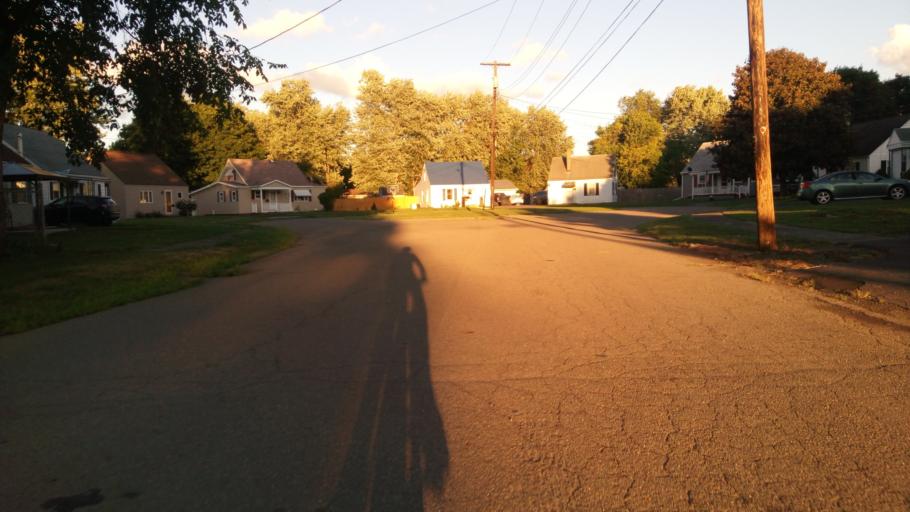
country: US
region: New York
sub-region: Chemung County
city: Southport
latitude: 42.0626
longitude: -76.8013
